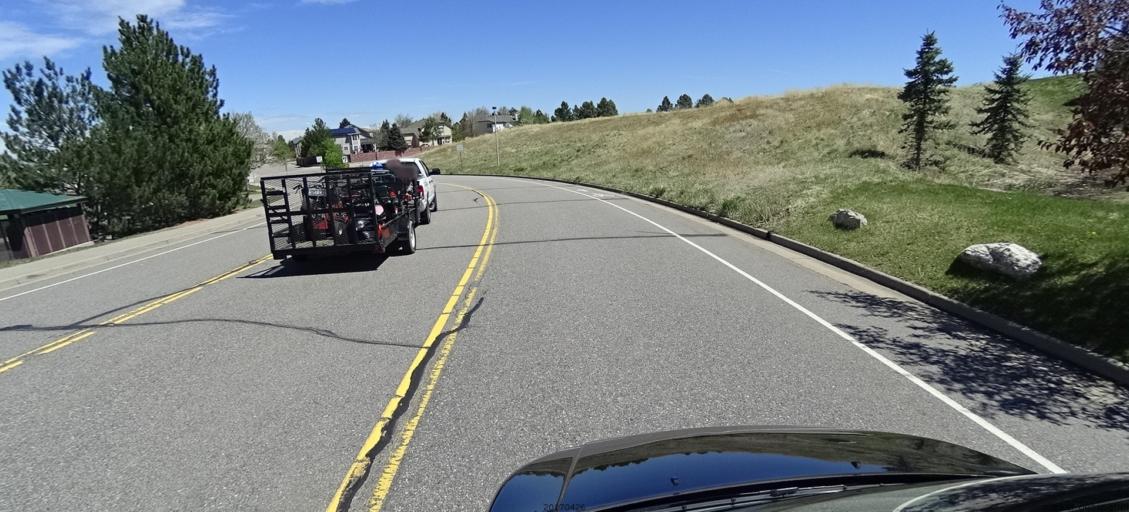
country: US
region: Colorado
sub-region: Adams County
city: Lone Tree
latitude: 39.5407
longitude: -104.8872
